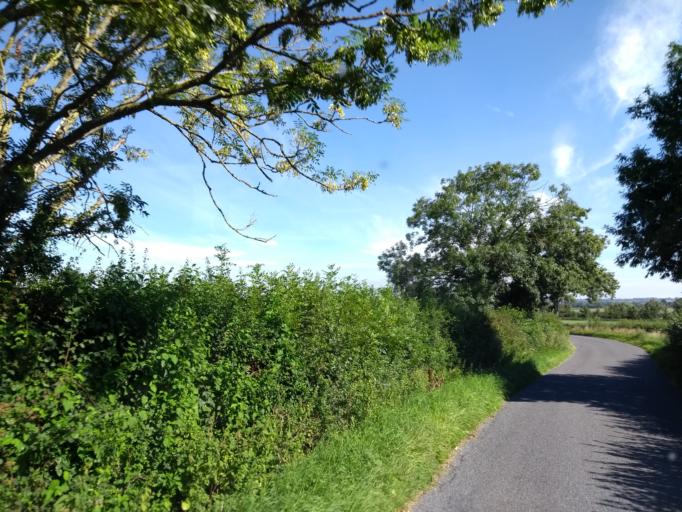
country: GB
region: England
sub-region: Somerset
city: Ilchester
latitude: 51.0848
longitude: -2.6433
